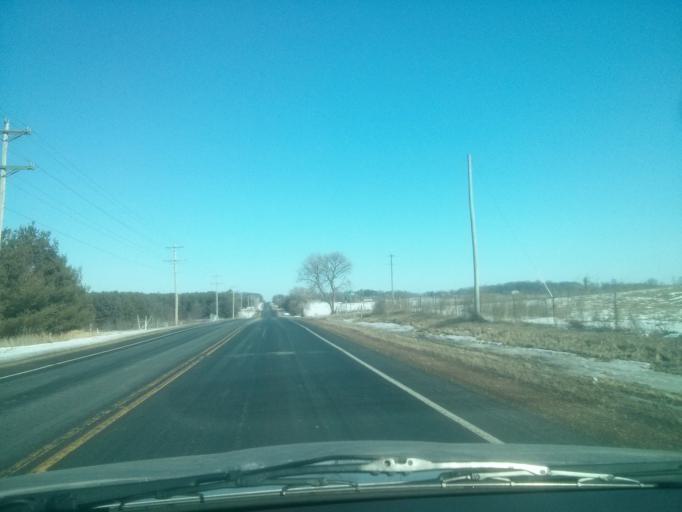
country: US
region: Minnesota
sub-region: Washington County
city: Bayport
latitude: 45.0711
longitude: -92.7361
